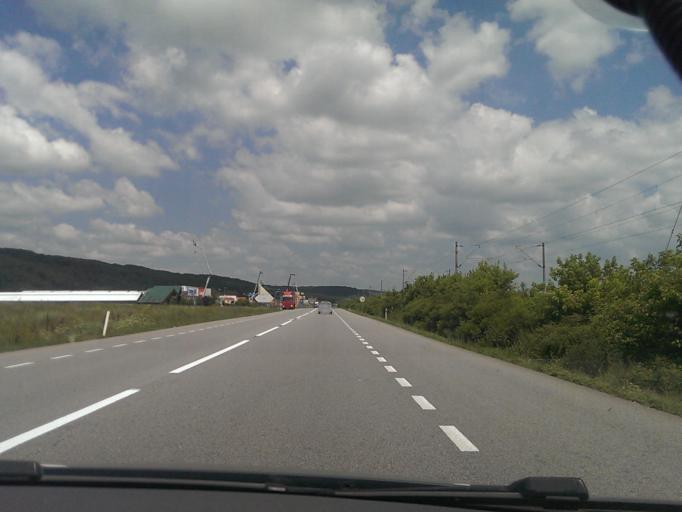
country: RO
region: Cluj
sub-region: Comuna Apahida
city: Apahida
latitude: 46.8256
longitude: 23.7449
